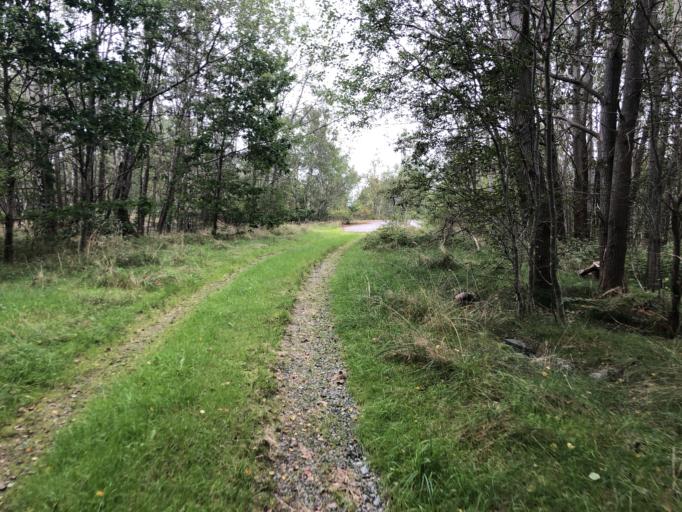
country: SE
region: Vaestra Goetaland
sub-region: Goteborg
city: Majorna
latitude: 57.7294
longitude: 11.8693
